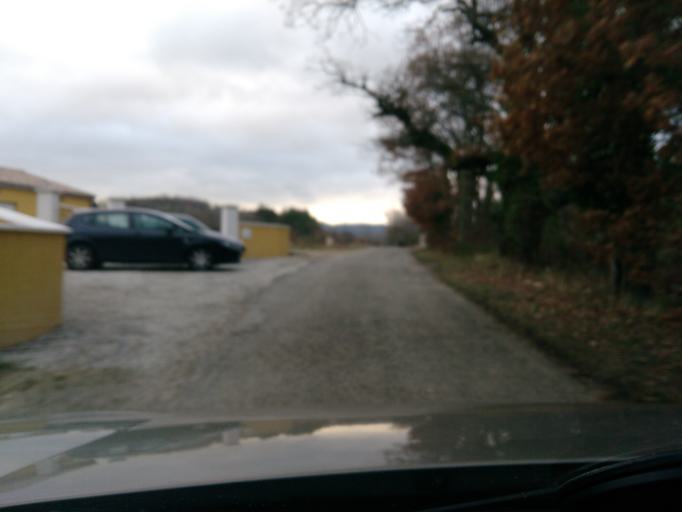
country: FR
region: Rhone-Alpes
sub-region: Departement de la Drome
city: Montboucher-sur-Jabron
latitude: 44.5350
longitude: 4.8156
